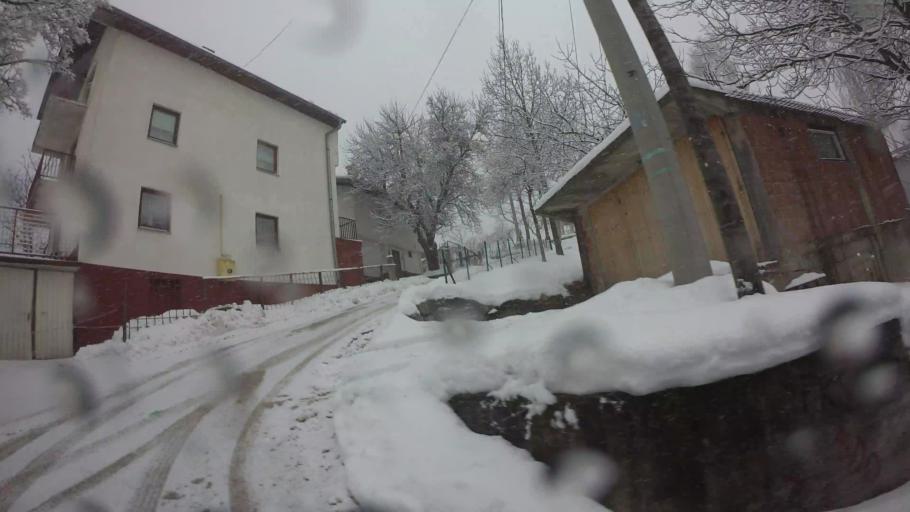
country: BA
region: Federation of Bosnia and Herzegovina
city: Kobilja Glava
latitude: 43.8492
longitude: 18.4561
